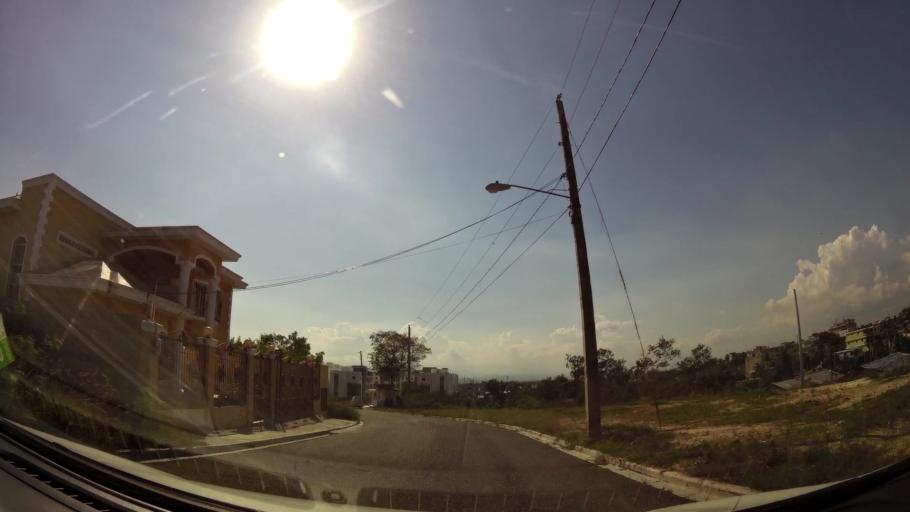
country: DO
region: Nacional
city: Santo Domingo
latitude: 18.4636
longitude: -69.9855
